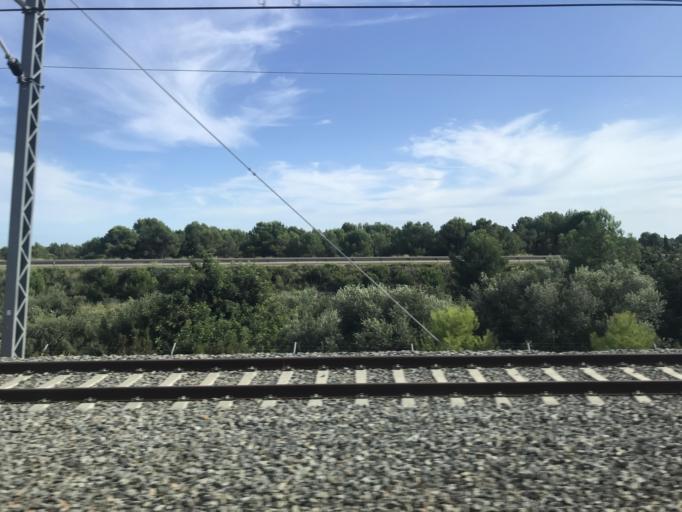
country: ES
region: Catalonia
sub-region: Provincia de Tarragona
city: Vilanova d'Escornalbou
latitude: 41.0464
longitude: 0.9688
